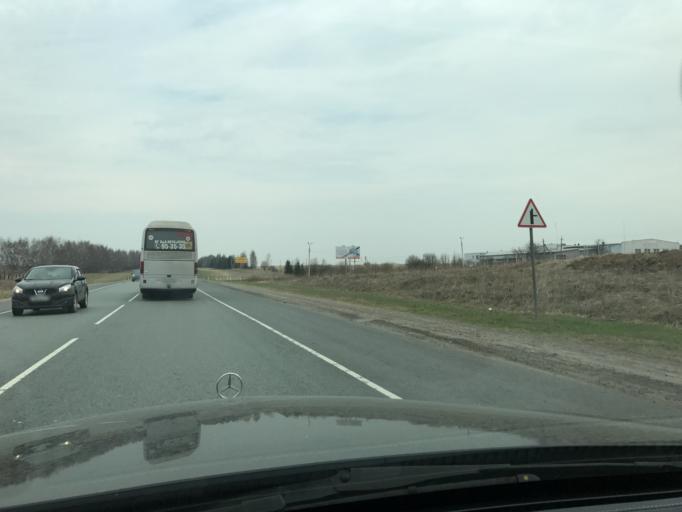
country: RU
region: Vladimir
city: Suzdal'
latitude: 56.3327
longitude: 40.4729
